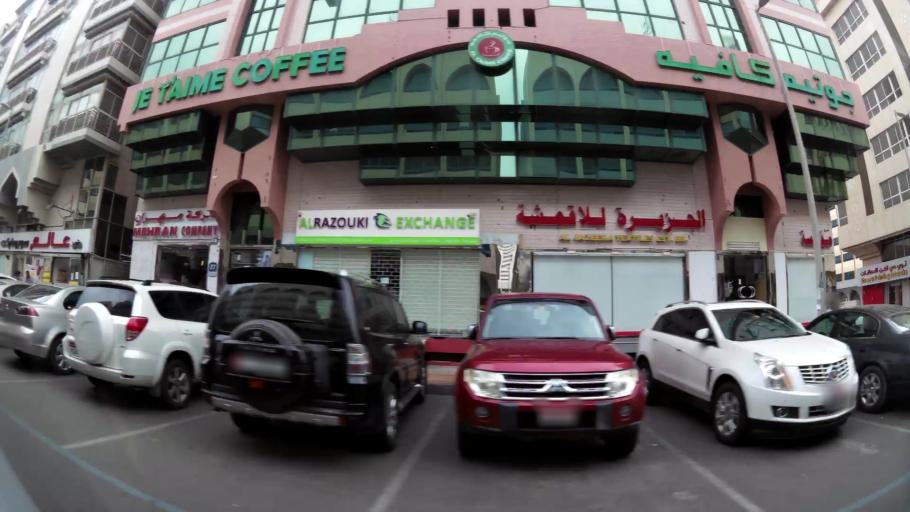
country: AE
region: Abu Dhabi
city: Abu Dhabi
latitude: 24.4800
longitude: 54.3658
